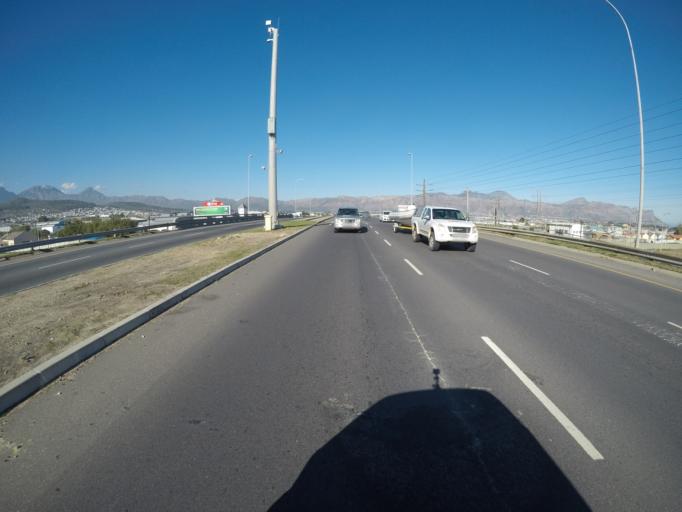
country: ZA
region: Western Cape
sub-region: Cape Winelands District Municipality
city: Stellenbosch
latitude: -34.1001
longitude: 18.8508
